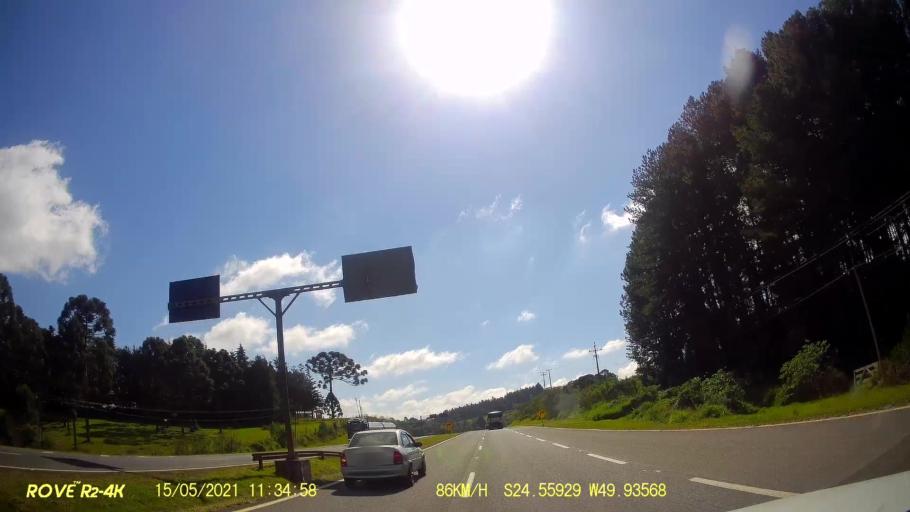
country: BR
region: Parana
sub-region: Pirai Do Sul
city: Pirai do Sul
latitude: -24.5593
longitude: -49.9357
